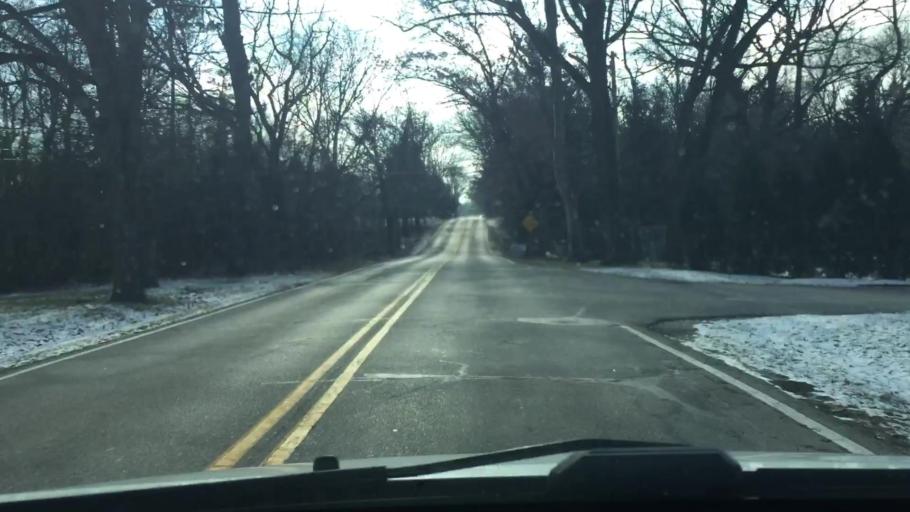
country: US
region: Wisconsin
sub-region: Waukesha County
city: Waukesha
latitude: 42.9816
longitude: -88.2872
